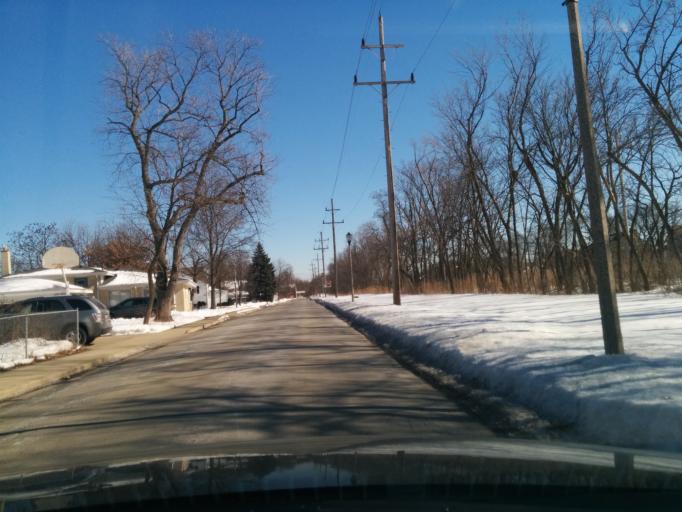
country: US
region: Illinois
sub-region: DuPage County
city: Elmhurst
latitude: 41.8865
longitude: -87.9578
